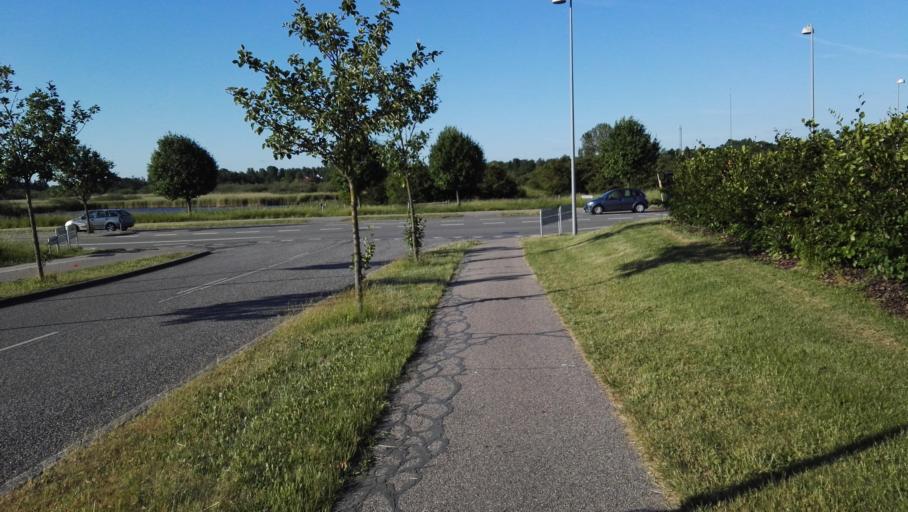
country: DK
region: Capital Region
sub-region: Ballerup Kommune
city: Malov
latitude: 55.7299
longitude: 12.3303
